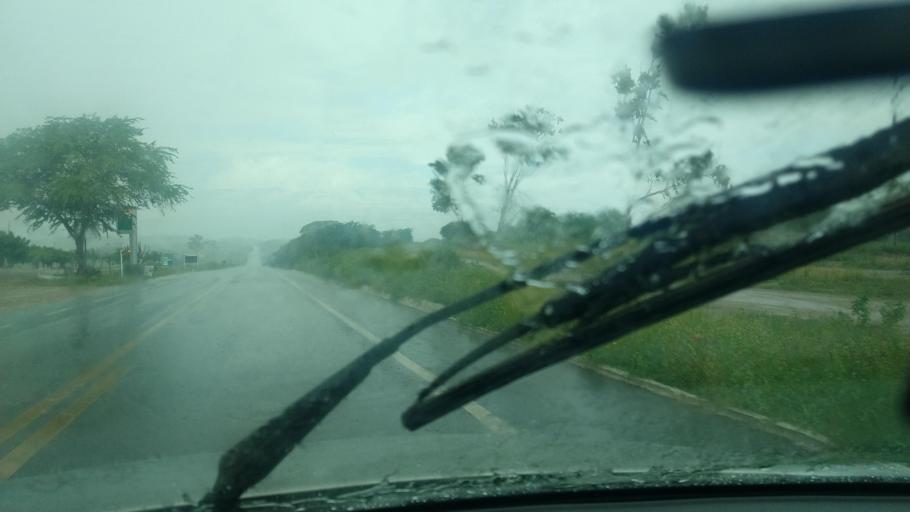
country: BR
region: Rio Grande do Norte
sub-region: Santa Cruz
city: Santa Cruz
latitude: -6.2077
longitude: -36.1869
